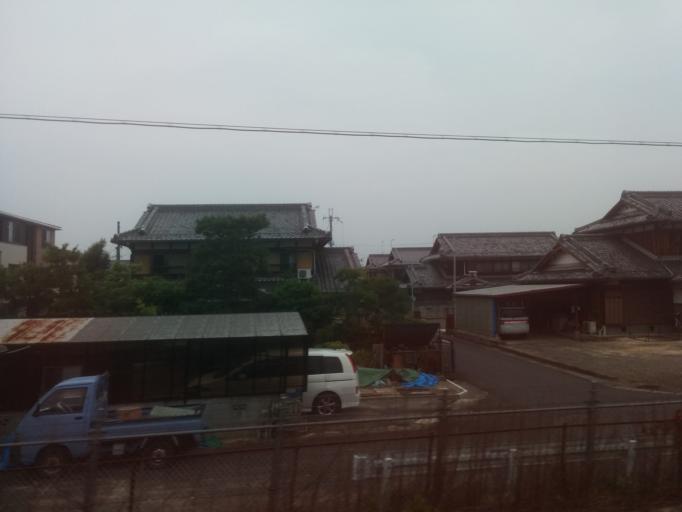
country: JP
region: Shiga Prefecture
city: Kusatsu
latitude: 35.0180
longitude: 135.9579
